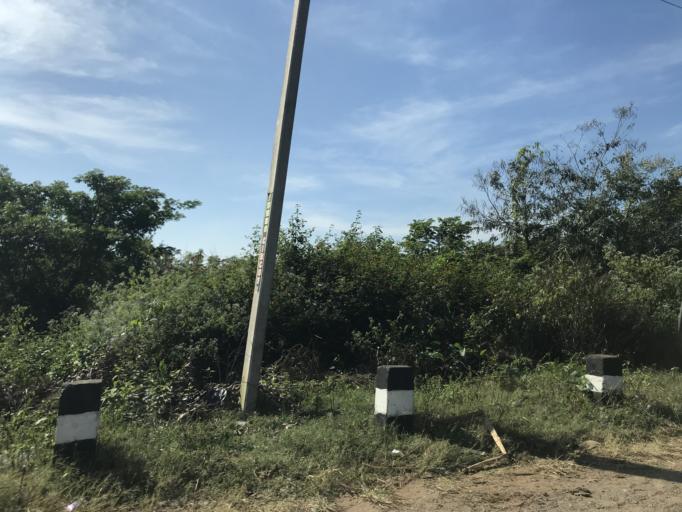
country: IN
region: Karnataka
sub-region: Mysore
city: Heggadadevankote
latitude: 12.1213
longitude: 76.4749
